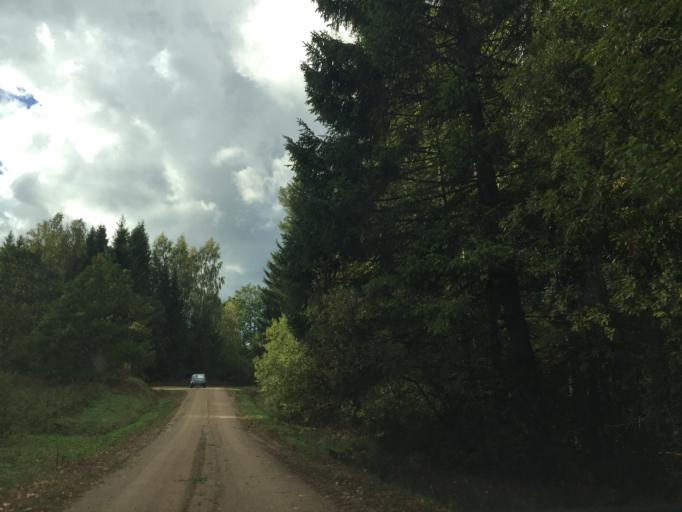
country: LV
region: Ligatne
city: Ligatne
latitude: 57.1053
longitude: 25.1324
